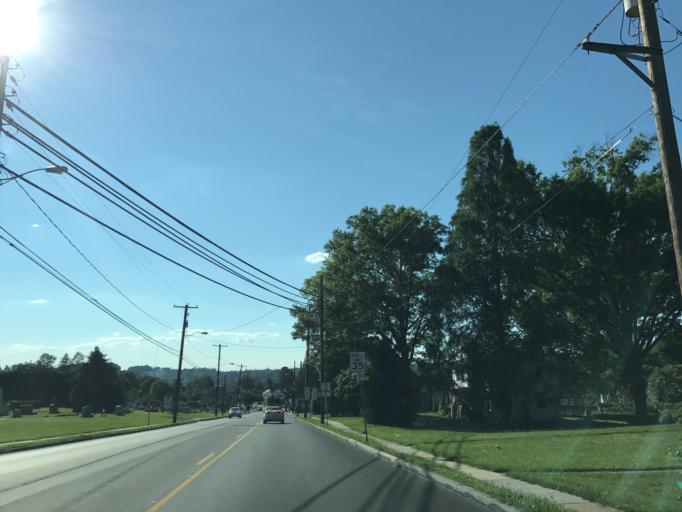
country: US
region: Pennsylvania
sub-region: Lancaster County
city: Elizabethtown
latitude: 40.1421
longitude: -76.5939
